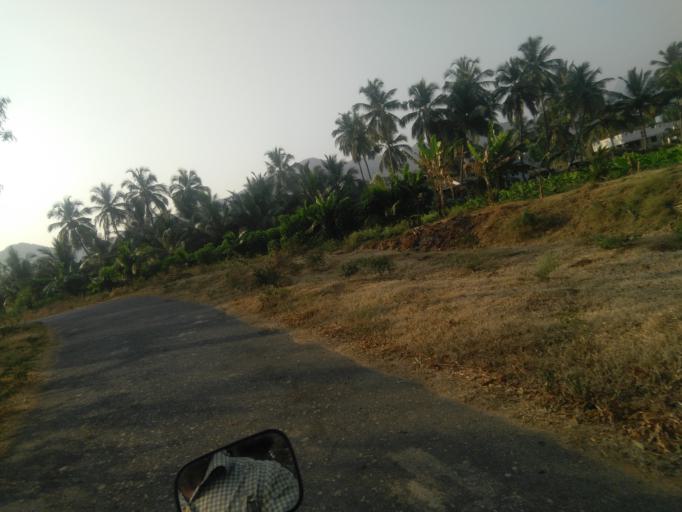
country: IN
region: Tamil Nadu
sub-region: Coimbatore
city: Karamadai
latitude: 11.2099
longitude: 76.8944
